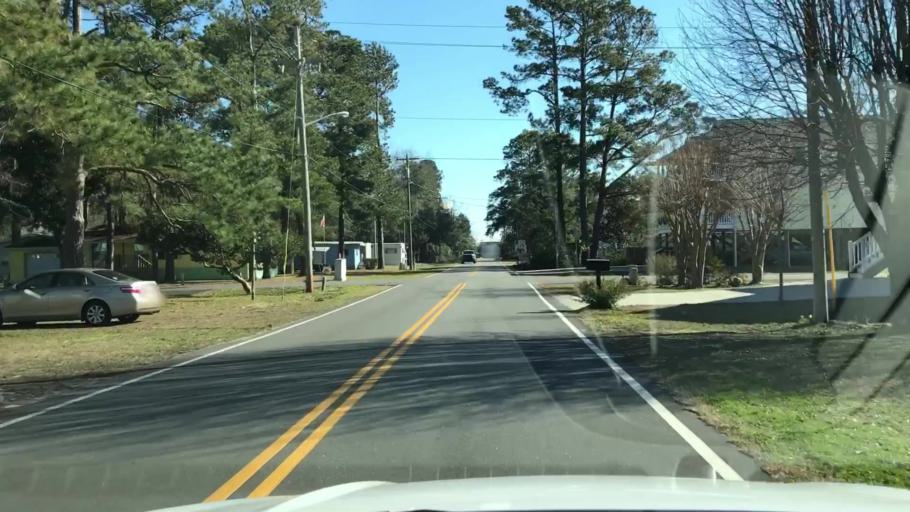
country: US
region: South Carolina
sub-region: Horry County
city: Garden City
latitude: 33.5898
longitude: -78.9961
